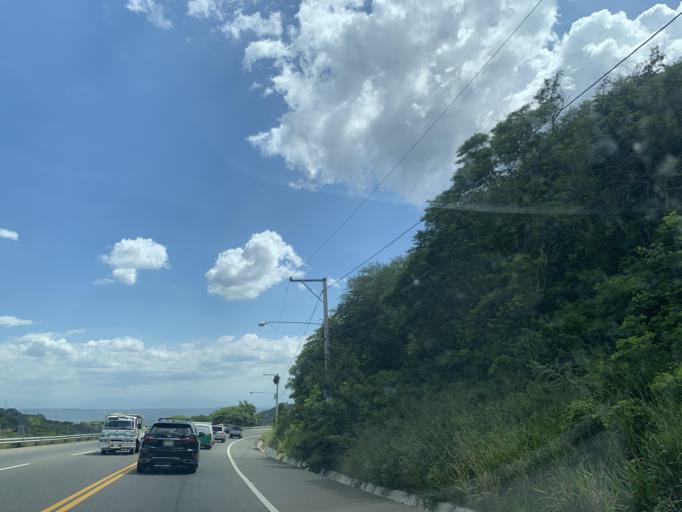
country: DO
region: Santiago
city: Villa Bisono
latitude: 19.6004
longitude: -70.8381
